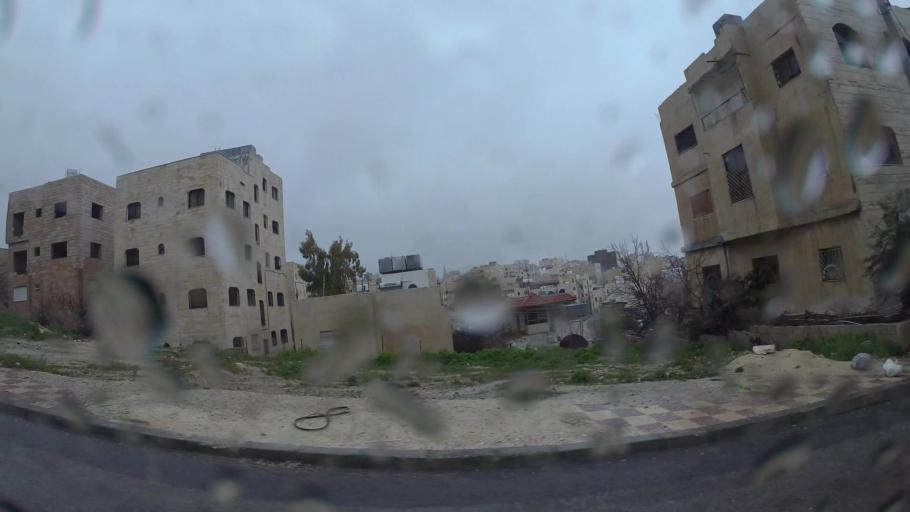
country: JO
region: Amman
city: Al Jubayhah
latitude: 32.0459
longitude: 35.8774
